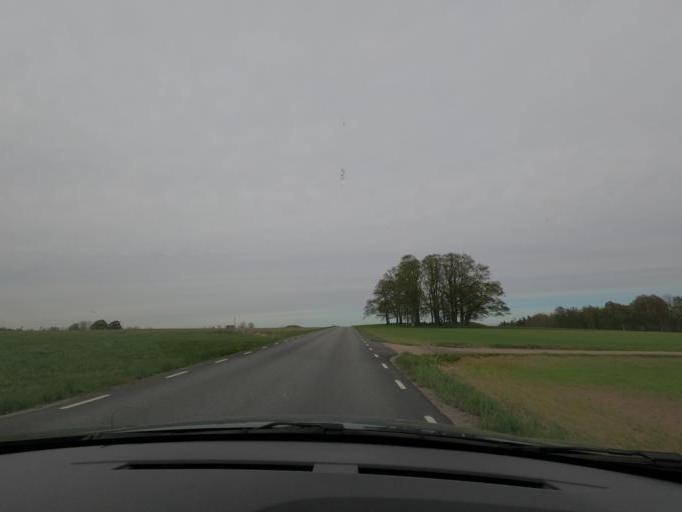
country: SE
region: Joenkoeping
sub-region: Varnamo Kommun
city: Bredaryd
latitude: 57.1429
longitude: 13.7160
